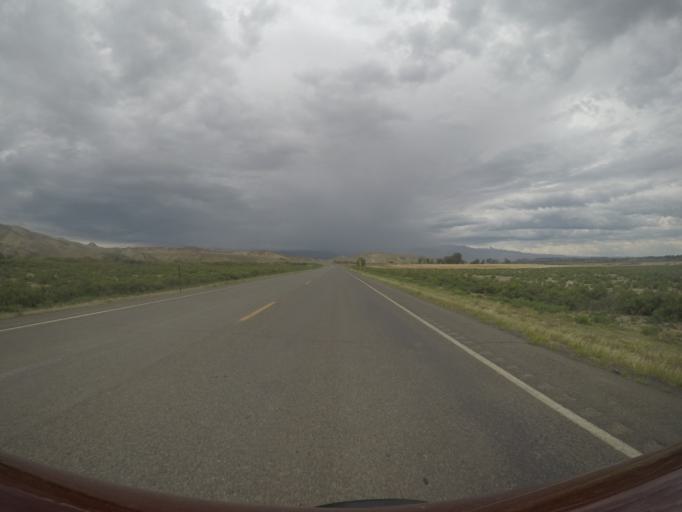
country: US
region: Wyoming
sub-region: Big Horn County
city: Lovell
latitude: 44.8776
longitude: -108.2976
